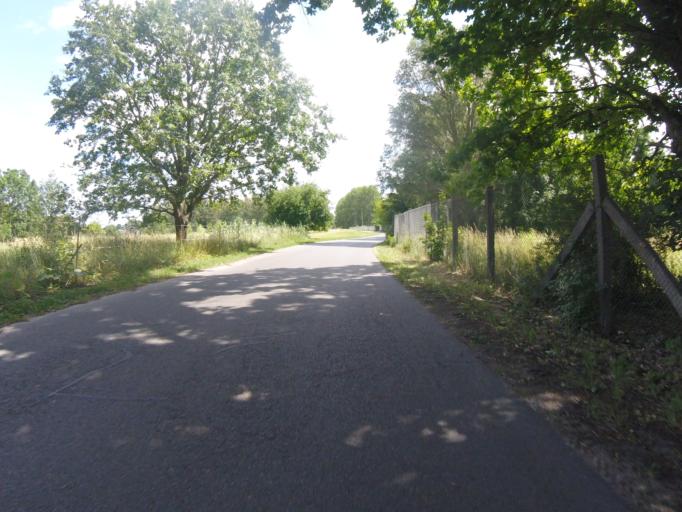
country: DE
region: Brandenburg
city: Mittenwalde
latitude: 52.2429
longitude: 13.5189
